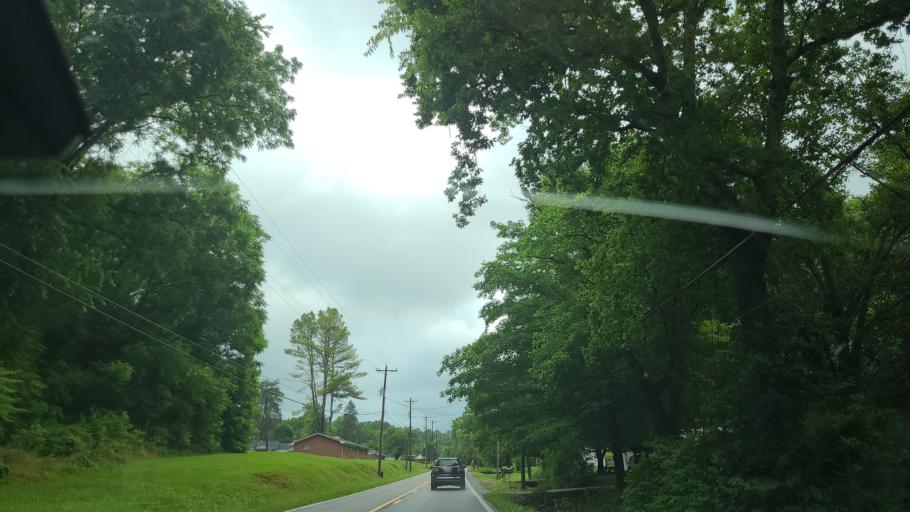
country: US
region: Tennessee
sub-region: Rhea County
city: Dayton
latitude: 35.4963
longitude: -84.9954
